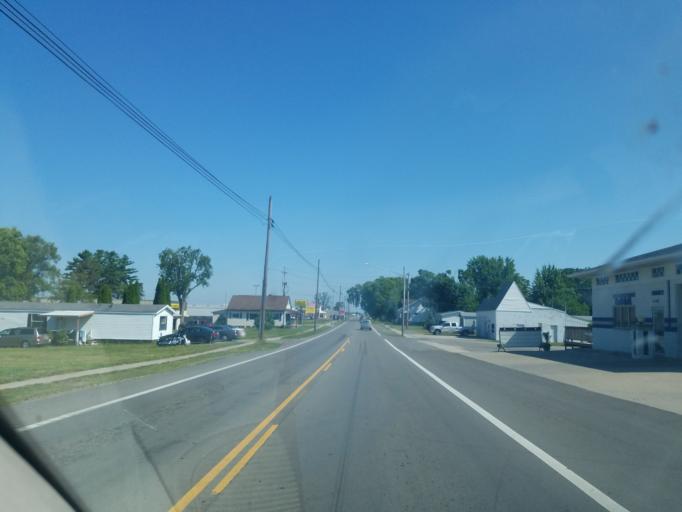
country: US
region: Ohio
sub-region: Logan County
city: Northwood
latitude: 40.4439
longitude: -83.8061
